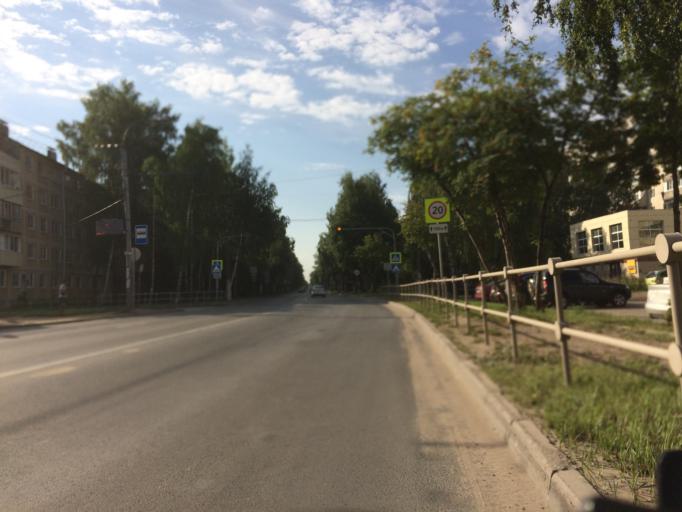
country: RU
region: Mariy-El
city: Medvedevo
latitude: 56.6390
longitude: 47.8321
